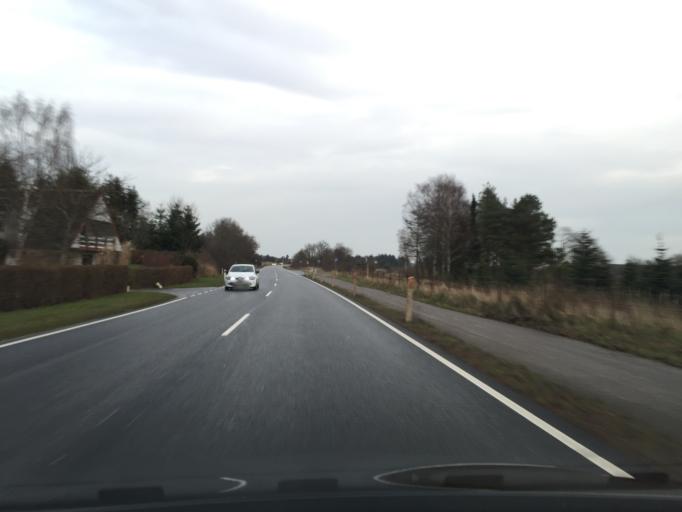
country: DK
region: Central Jutland
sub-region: Viborg Kommune
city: Bjerringbro
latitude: 56.3657
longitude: 9.6106
